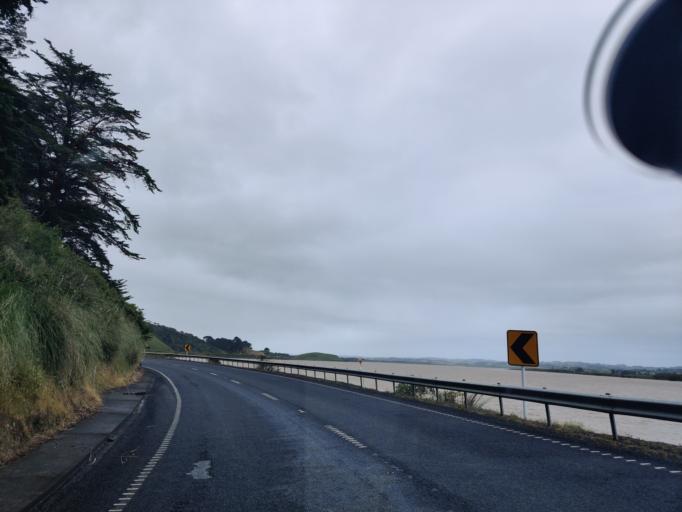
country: NZ
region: Northland
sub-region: Kaipara District
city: Dargaville
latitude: -36.0594
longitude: 173.9668
